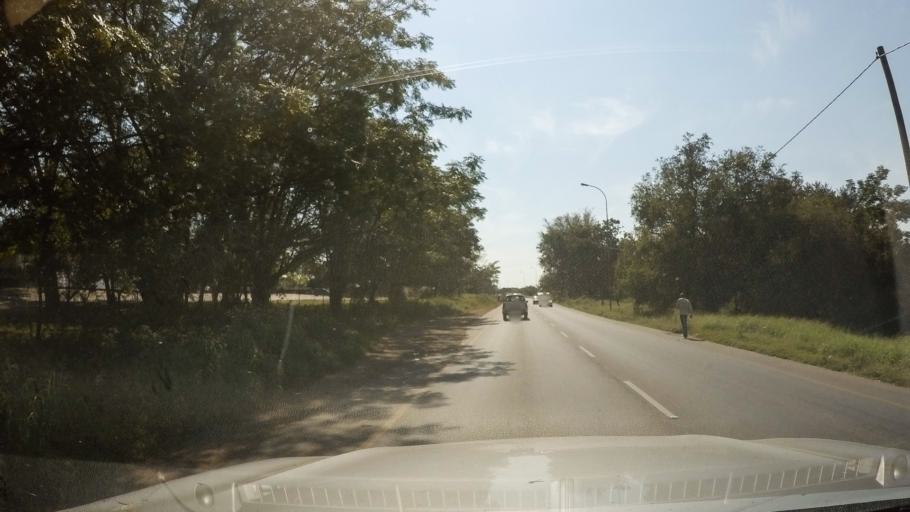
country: BW
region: South East
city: Lobatse
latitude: -25.2233
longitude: 25.6784
